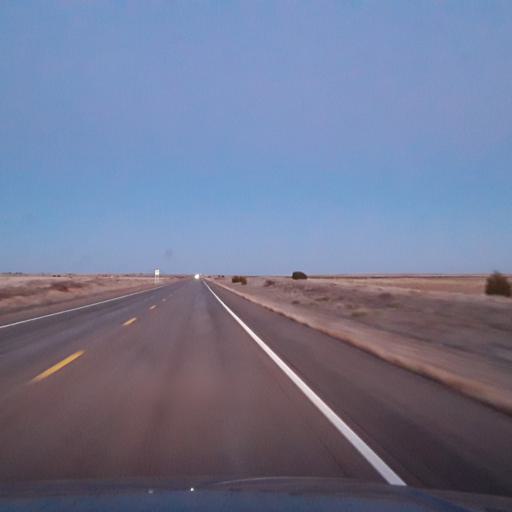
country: US
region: New Mexico
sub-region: Guadalupe County
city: Santa Rosa
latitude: 34.7557
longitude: -105.0001
